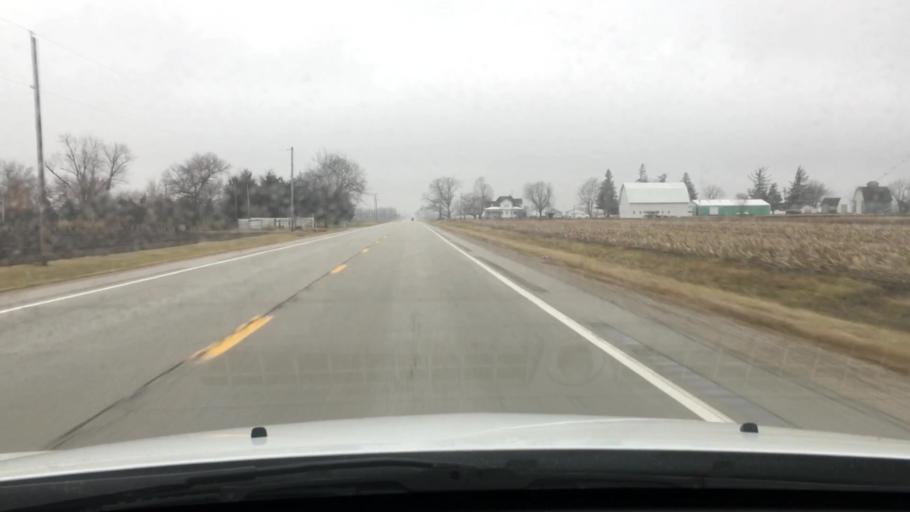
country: US
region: Illinois
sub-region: Livingston County
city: Flanagan
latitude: 40.8704
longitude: -88.8796
